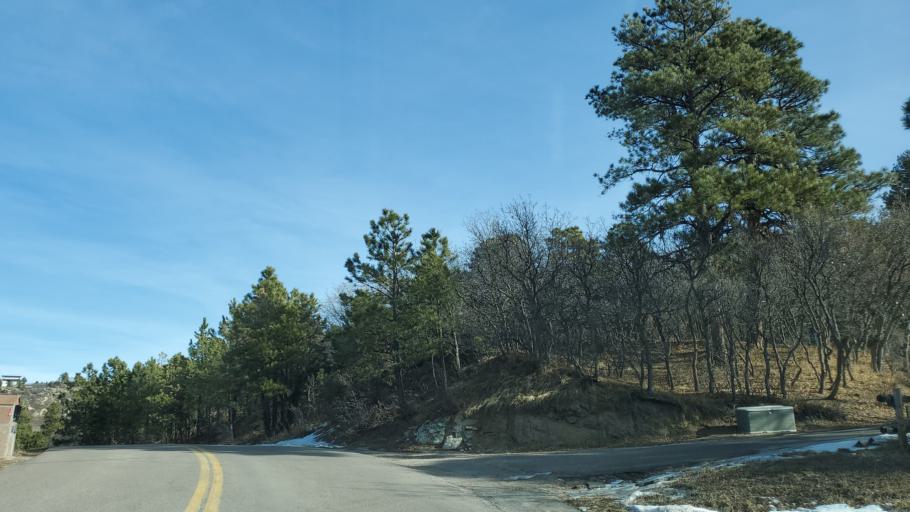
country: US
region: Colorado
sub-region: Douglas County
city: Castle Pines
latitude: 39.4306
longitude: -104.8716
